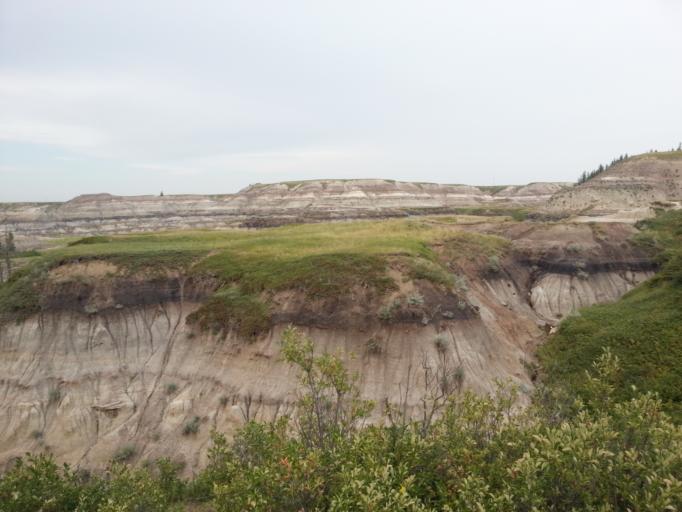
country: CA
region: Alberta
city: Three Hills
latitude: 51.4172
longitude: -112.8863
